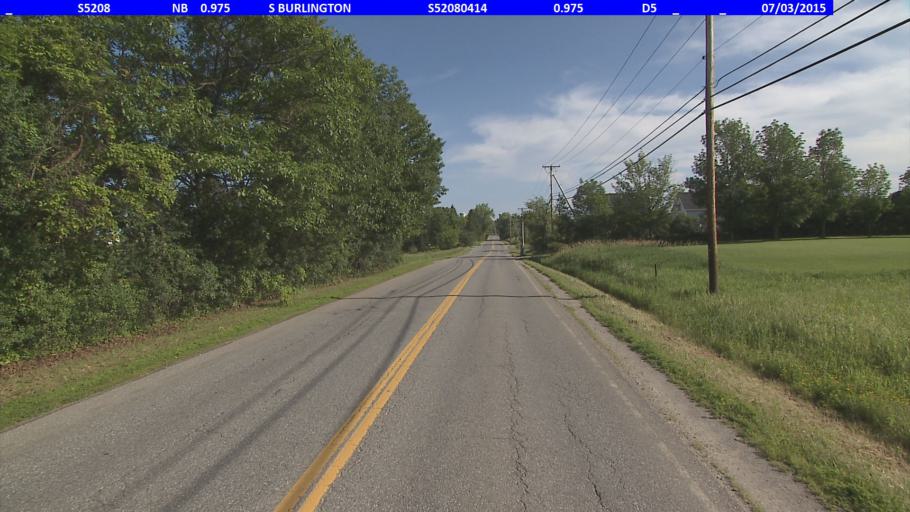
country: US
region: Vermont
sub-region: Chittenden County
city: South Burlington
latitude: 44.4248
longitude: -73.1740
